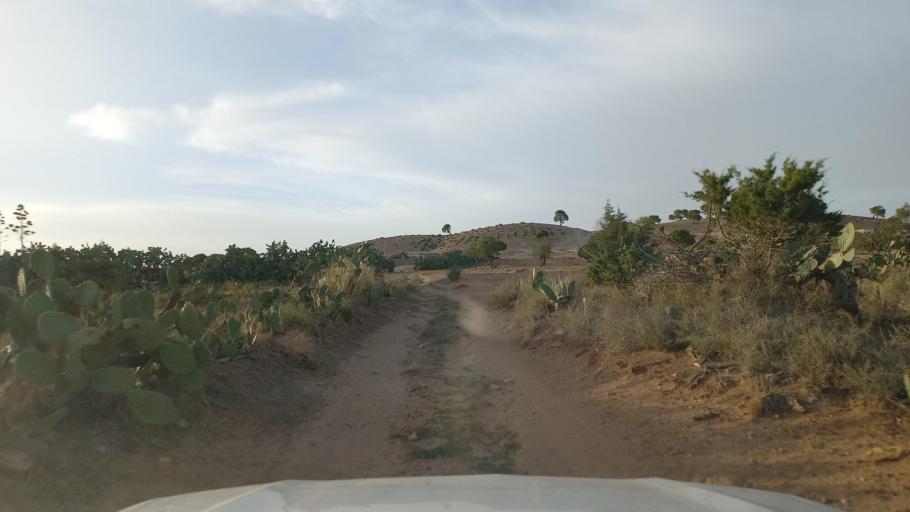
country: TN
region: Al Qasrayn
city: Sbiba
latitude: 35.4113
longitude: 8.9074
